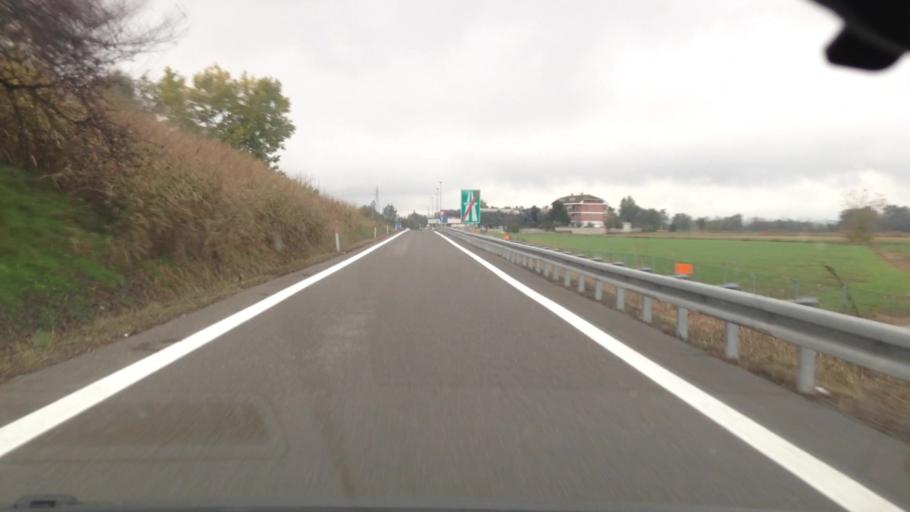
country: IT
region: Piedmont
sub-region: Provincia di Asti
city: Villanova d'Asti
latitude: 44.9549
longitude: 7.9158
